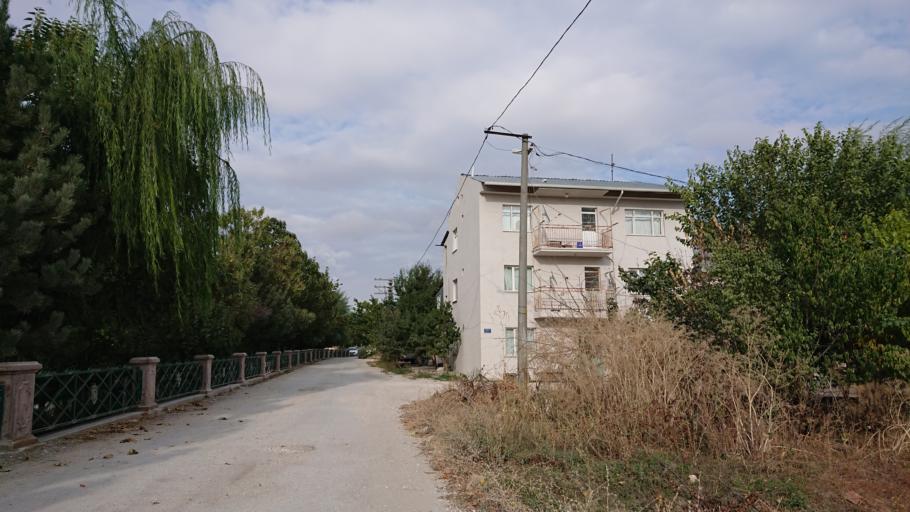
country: TR
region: Eskisehir
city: Eskisehir
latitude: 39.7648
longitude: 30.4871
